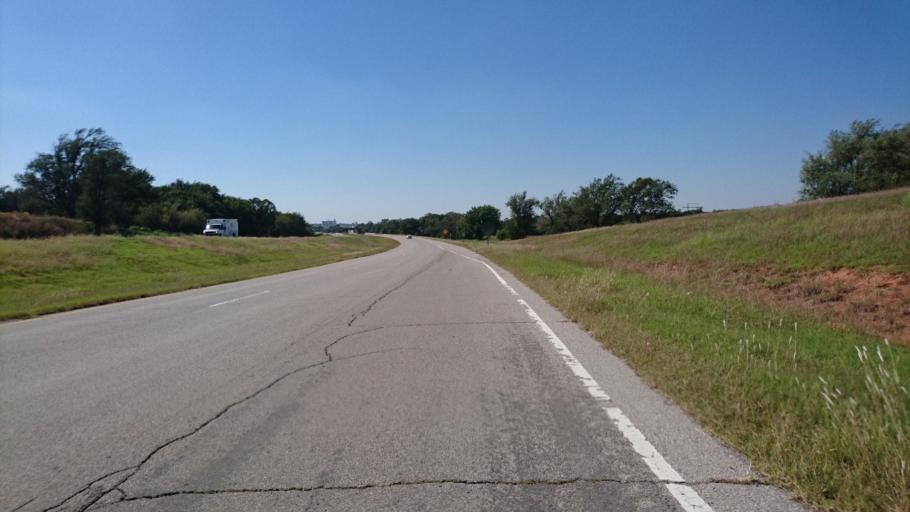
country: US
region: Oklahoma
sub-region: Custer County
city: Clinton
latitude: 35.5159
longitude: -98.9253
